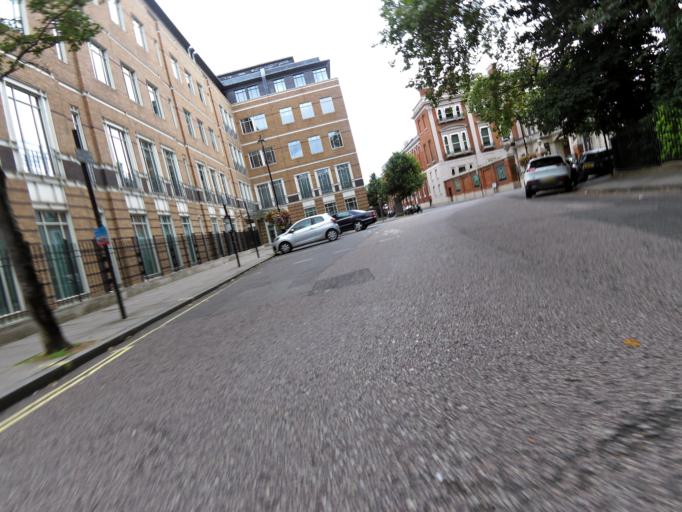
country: GB
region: England
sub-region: Greater London
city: Camden Town
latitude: 51.5167
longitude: -0.1532
